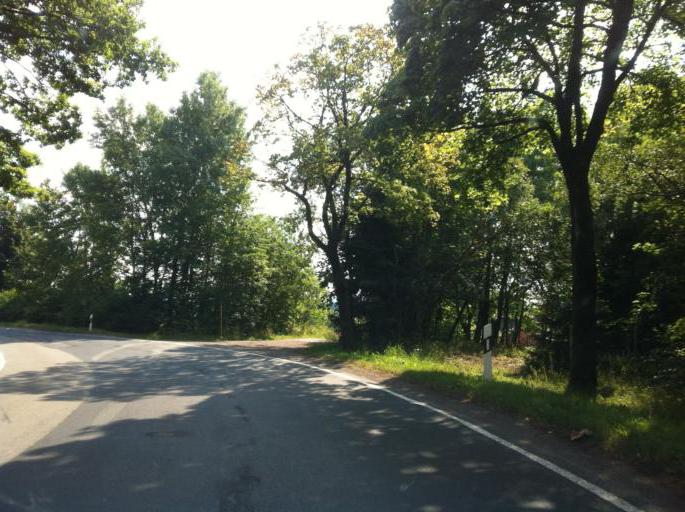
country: DE
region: Thuringia
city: Grossbreitenbach
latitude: 50.5938
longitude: 10.9848
